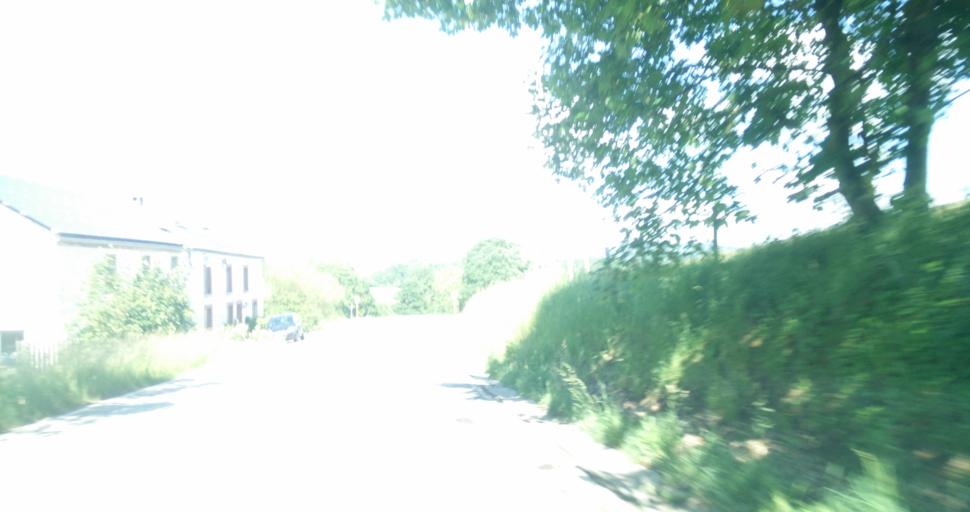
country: BE
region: Wallonia
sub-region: Province du Luxembourg
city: Rendeux
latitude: 50.1886
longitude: 5.4910
